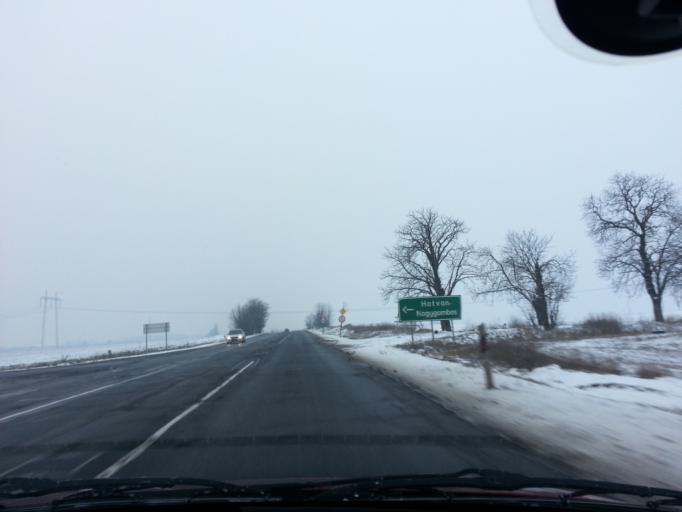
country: HU
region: Heves
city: Hered
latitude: 47.6952
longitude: 19.6646
